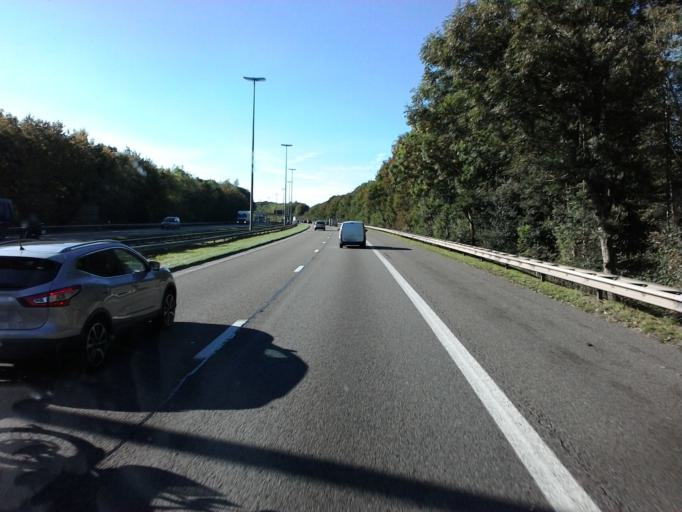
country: BE
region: Wallonia
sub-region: Province du Luxembourg
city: Arlon
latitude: 49.6665
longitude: 5.8054
